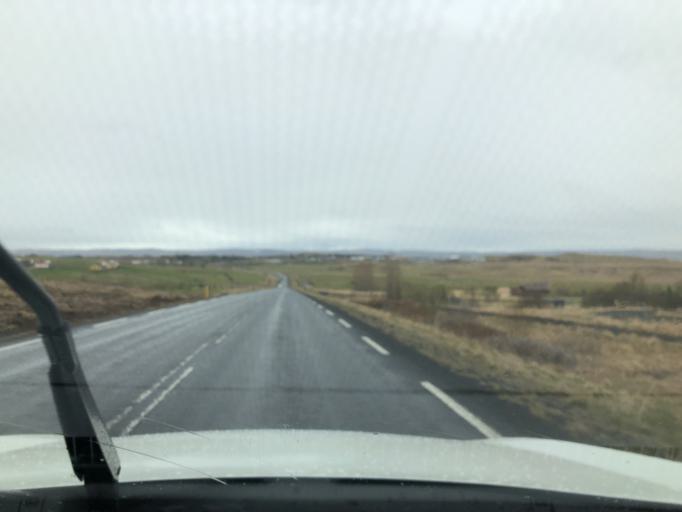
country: IS
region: South
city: Selfoss
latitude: 64.1762
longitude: -20.4793
